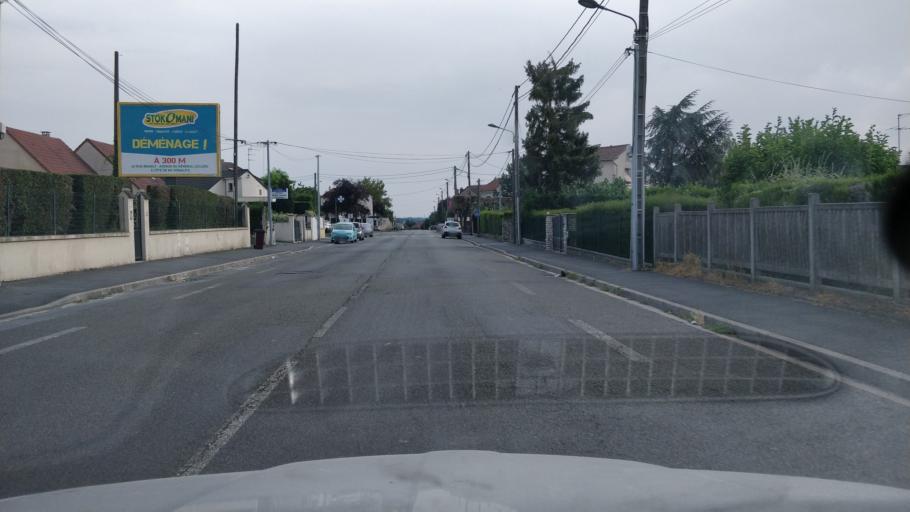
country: FR
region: Ile-de-France
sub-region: Departement de Seine-et-Marne
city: Thorigny-sur-Marne
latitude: 48.8893
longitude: 2.7051
